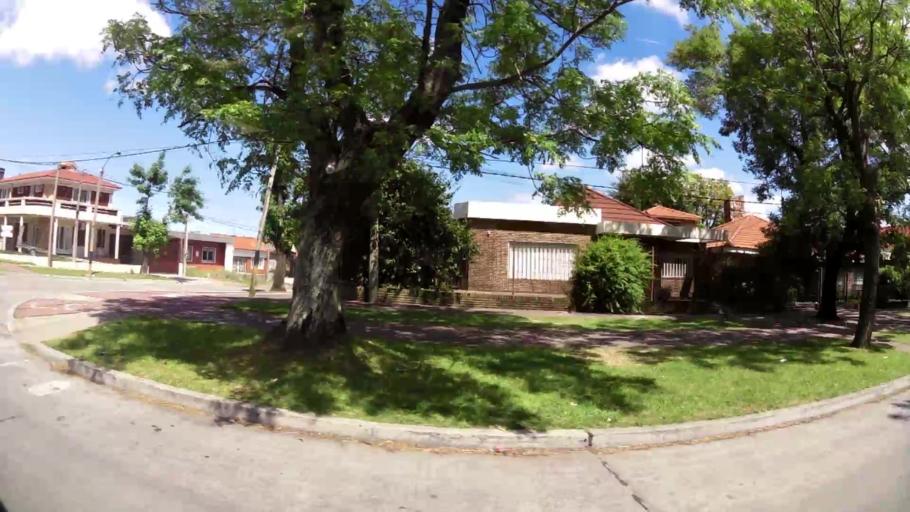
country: UY
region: Montevideo
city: Montevideo
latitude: -34.8526
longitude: -56.1490
